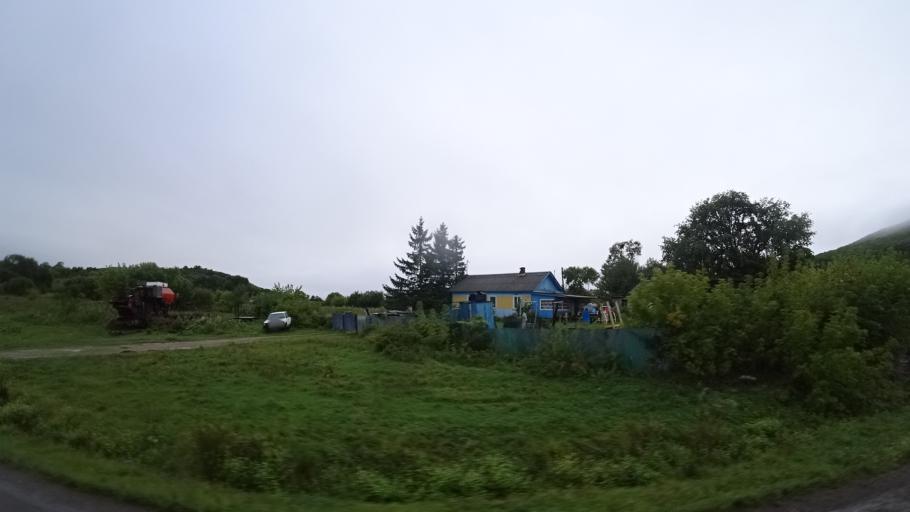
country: RU
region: Primorskiy
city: Monastyrishche
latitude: 44.2592
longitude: 132.4194
